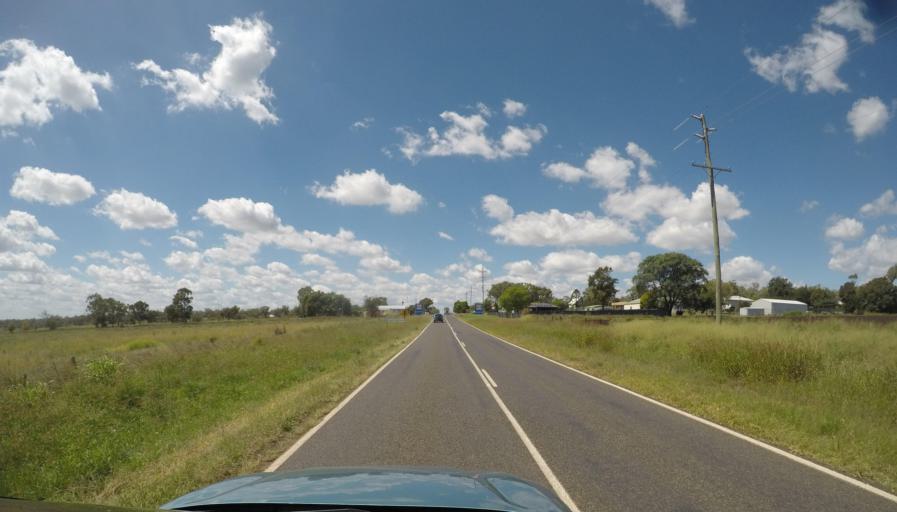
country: AU
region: Queensland
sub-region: Toowoomba
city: Oakey
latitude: -27.5557
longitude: 151.7163
